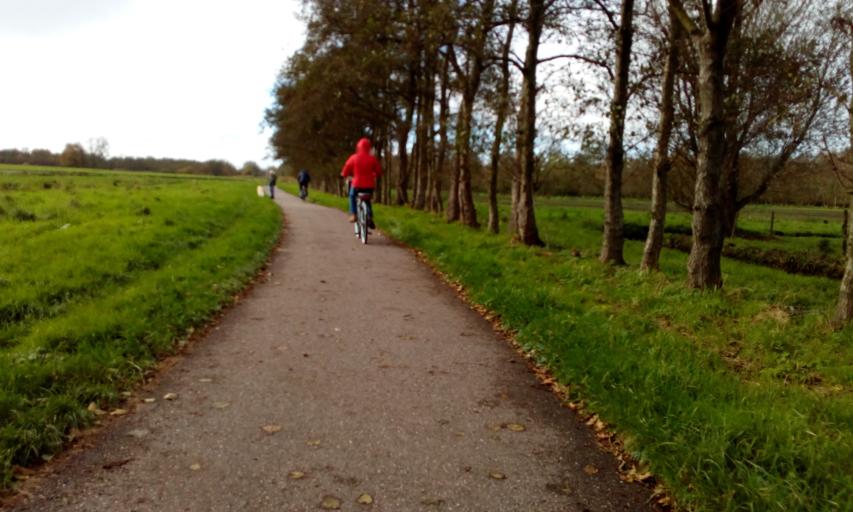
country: NL
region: South Holland
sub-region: Gemeente Pijnacker-Nootdorp
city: Pijnacker
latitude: 51.9813
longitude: 4.4170
